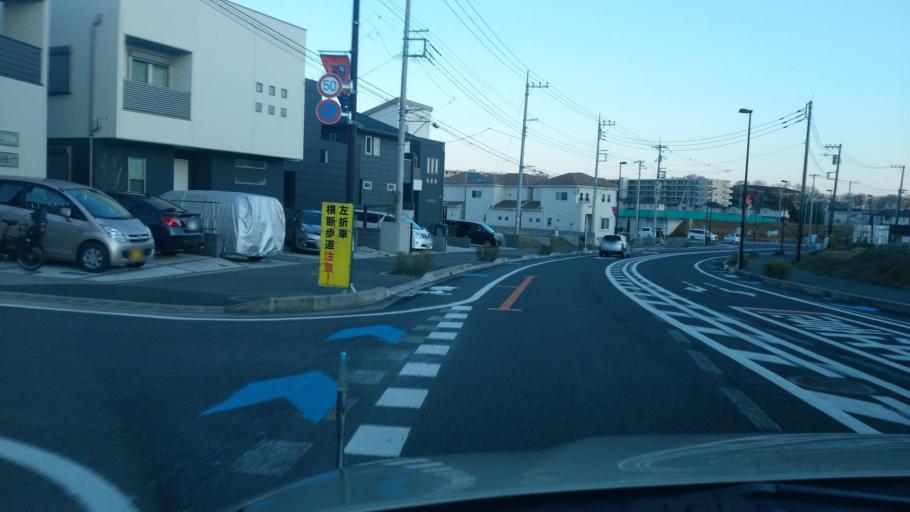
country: JP
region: Saitama
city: Ageoshimo
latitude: 35.9316
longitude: 139.5742
